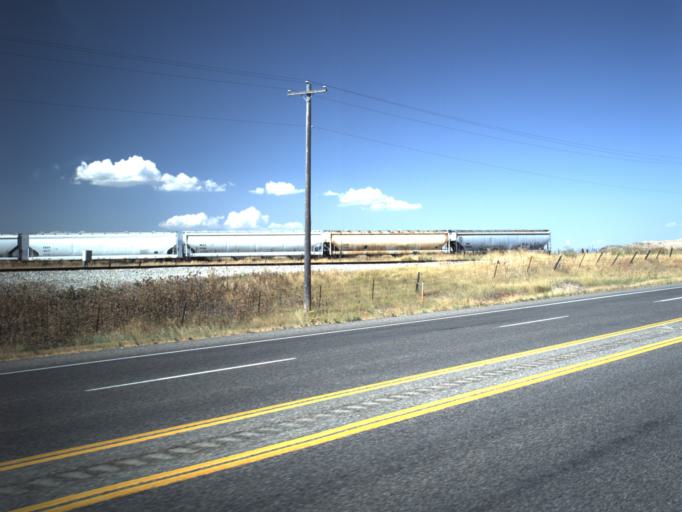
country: US
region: Utah
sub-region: Cache County
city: Lewiston
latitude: 41.9788
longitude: -111.8127
